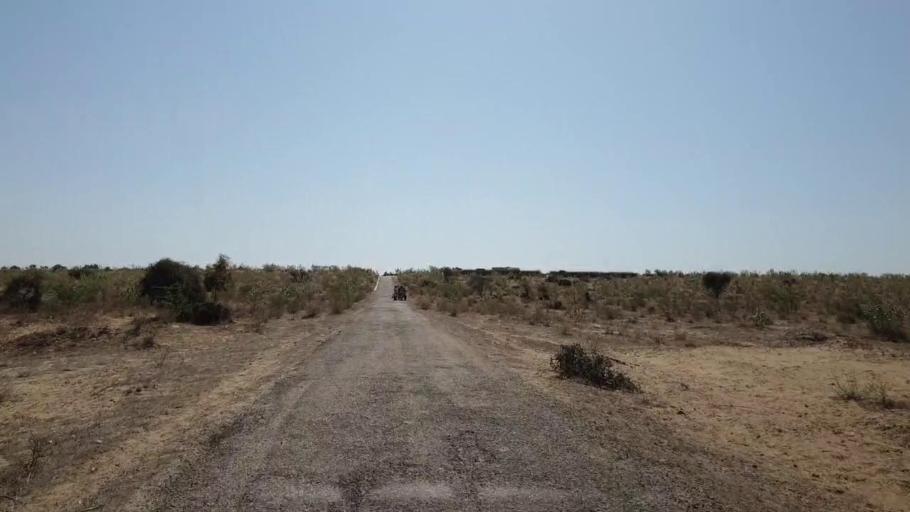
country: PK
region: Sindh
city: Nabisar
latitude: 25.0786
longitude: 69.9813
